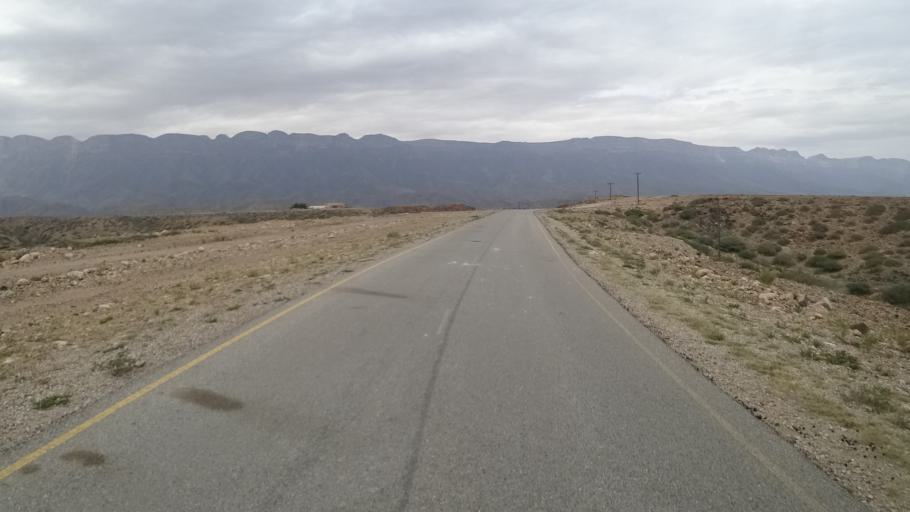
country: OM
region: Zufar
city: Salalah
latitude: 17.1480
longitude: 55.0049
